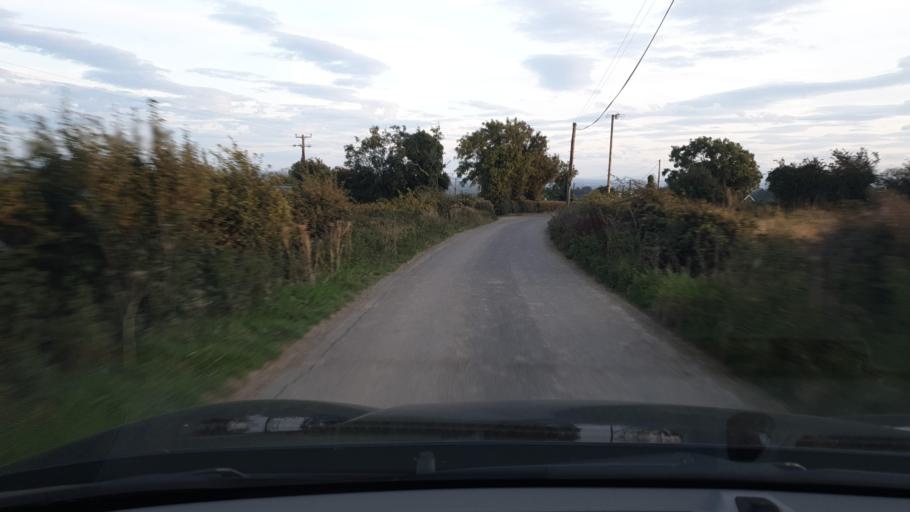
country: IE
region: Leinster
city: Balrothery
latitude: 53.5701
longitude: -6.2416
